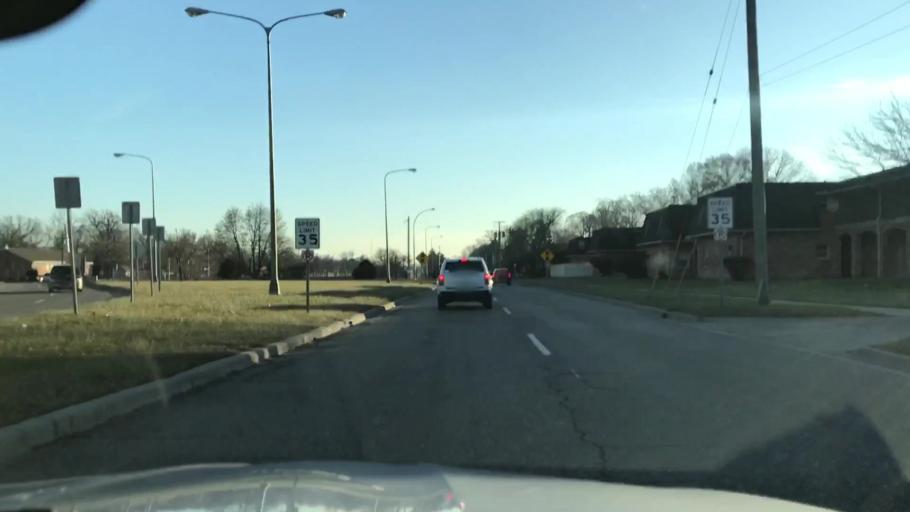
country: US
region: Michigan
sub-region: Oakland County
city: Madison Heights
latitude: 42.5006
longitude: -83.1180
